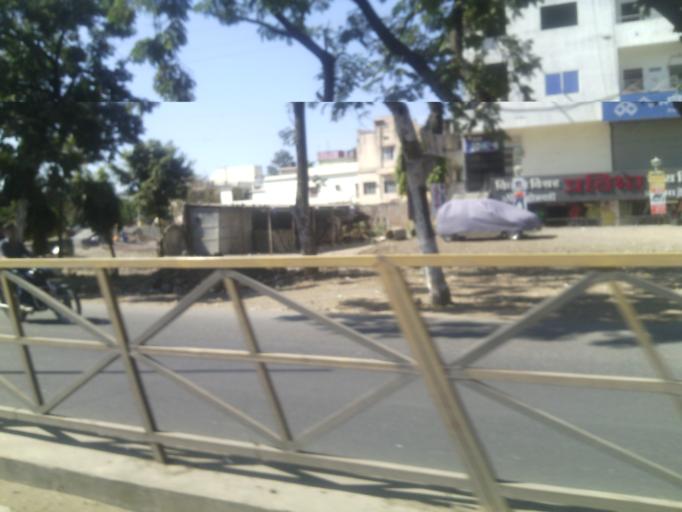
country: IN
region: Madhya Pradesh
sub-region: Dewas
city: Dewas
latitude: 22.9584
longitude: 76.0426
